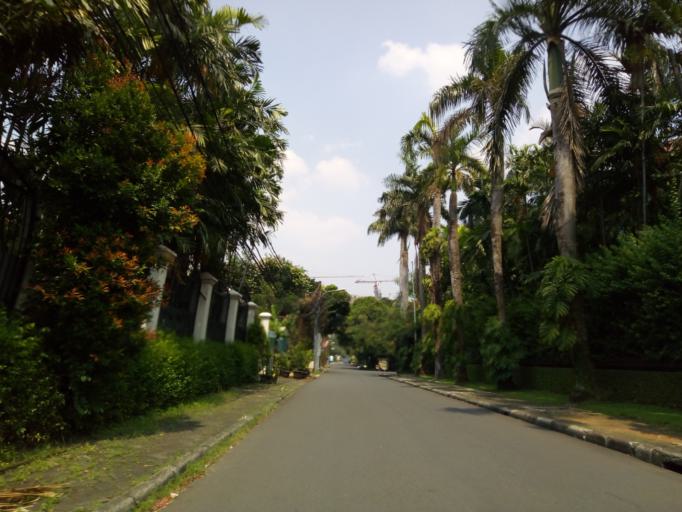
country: ID
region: Jakarta Raya
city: Jakarta
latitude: -6.2030
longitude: 106.8399
